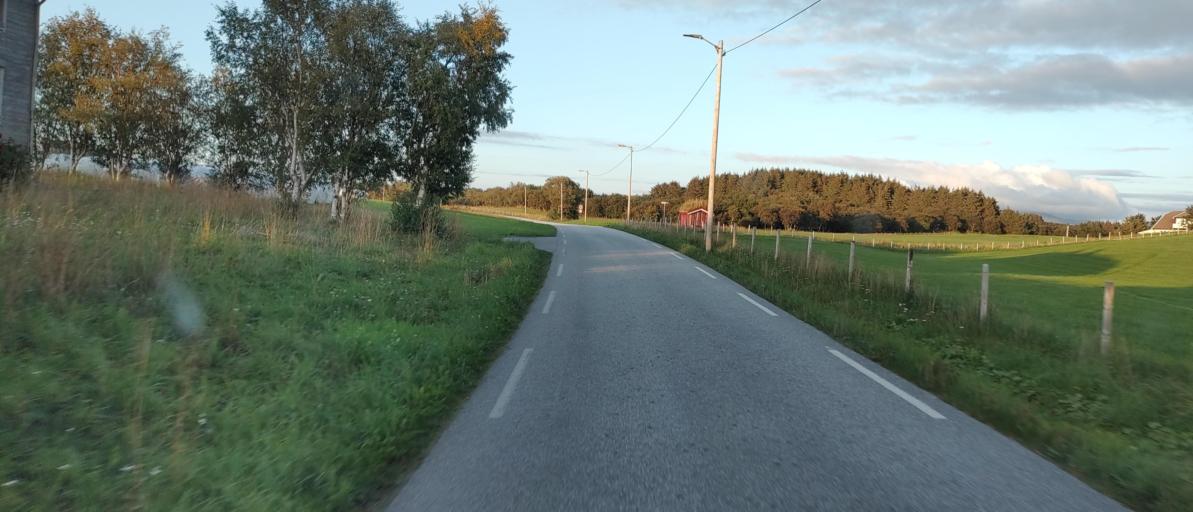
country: NO
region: More og Romsdal
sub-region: Fraena
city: Elnesvagen
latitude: 62.9908
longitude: 7.2153
